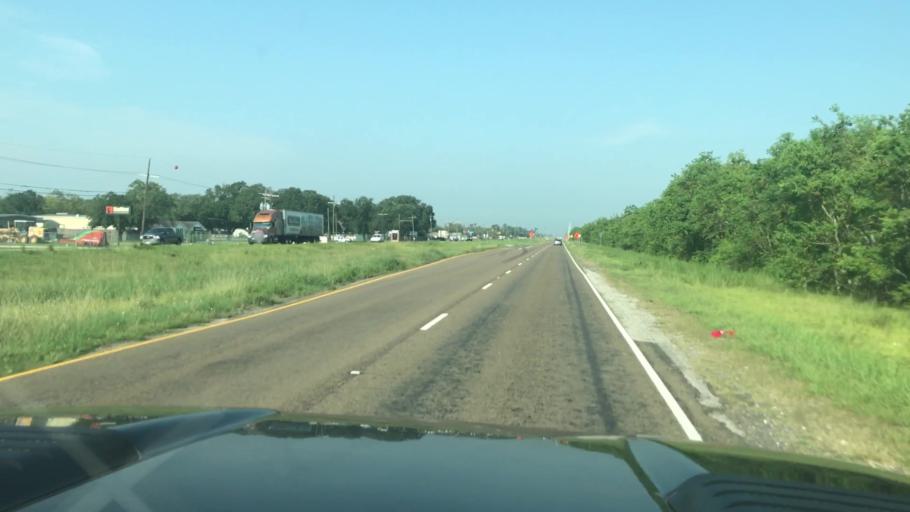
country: US
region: Texas
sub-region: Jefferson County
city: Bevil Oaks
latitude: 30.0646
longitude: -94.2119
